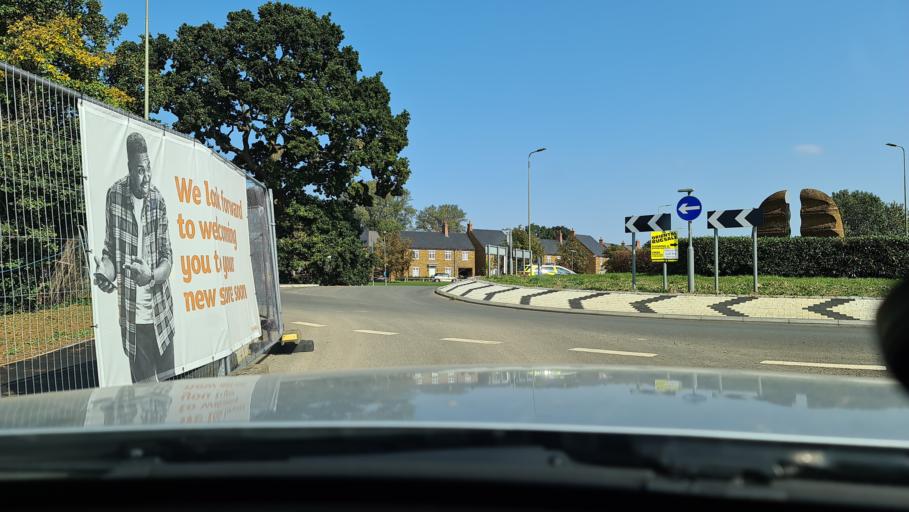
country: GB
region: England
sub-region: Oxfordshire
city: Hanwell
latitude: 52.0790
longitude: -1.3684
